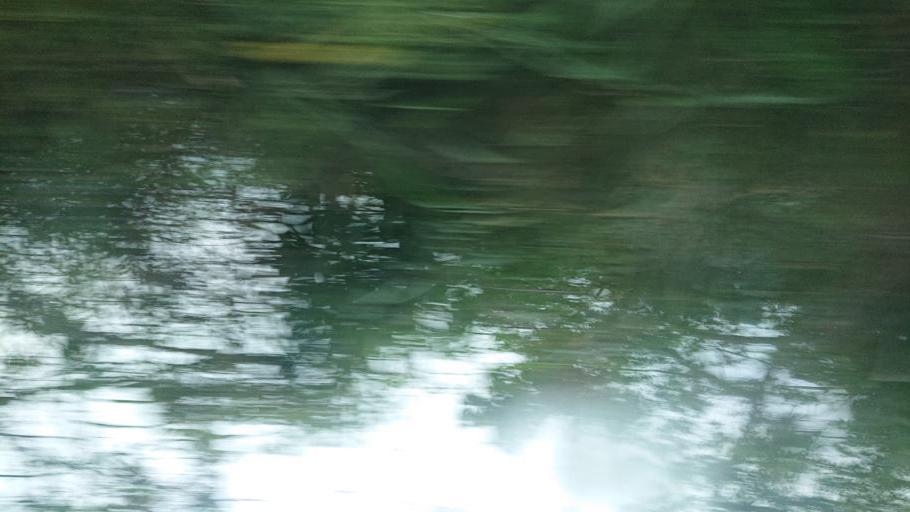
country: TW
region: Taiwan
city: Lugu
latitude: 23.5987
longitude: 120.7137
